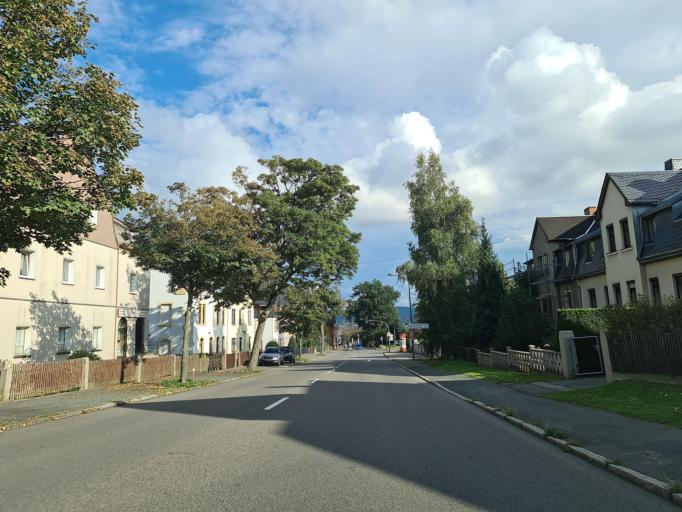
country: DE
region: Saxony
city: Auerbach
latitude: 50.5174
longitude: 12.3841
